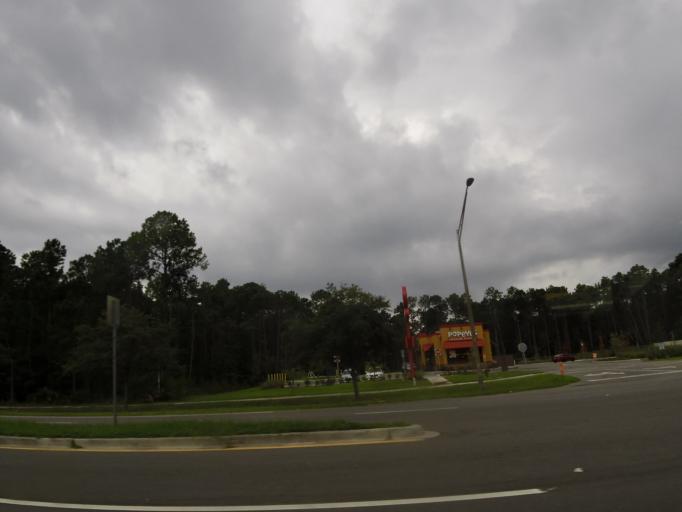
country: US
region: Florida
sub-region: Clay County
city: Bellair-Meadowbrook Terrace
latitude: 30.1964
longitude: -81.7751
